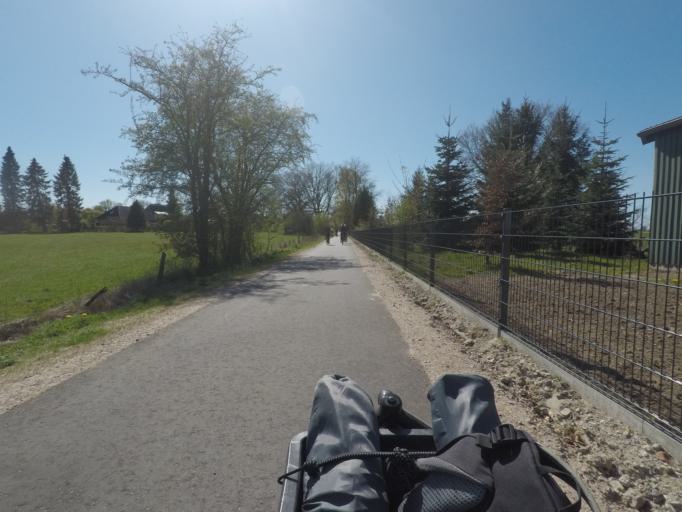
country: DE
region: Schleswig-Holstein
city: Siek
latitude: 53.6094
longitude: 10.2884
